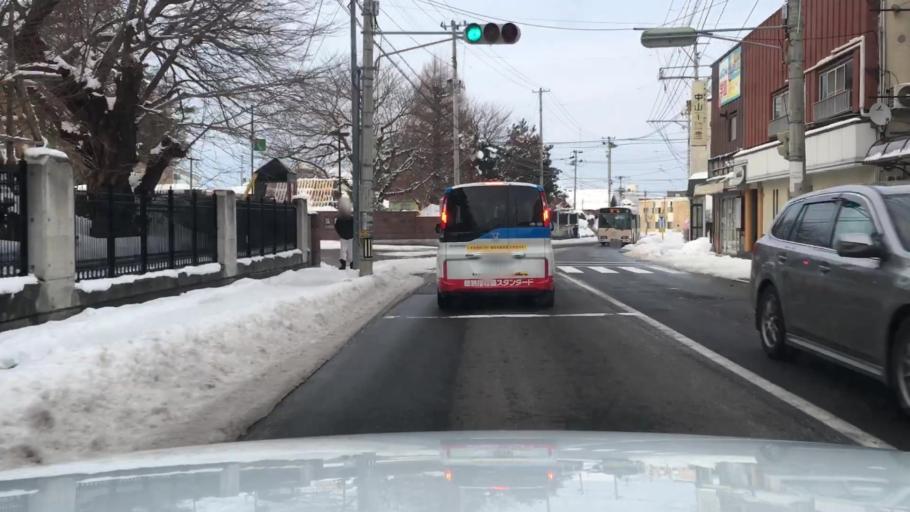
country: JP
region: Aomori
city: Hirosaki
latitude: 40.5895
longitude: 140.4740
